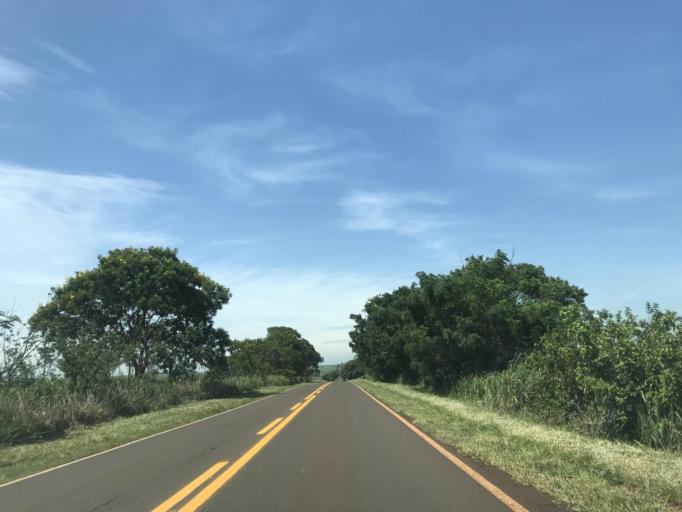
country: BR
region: Parana
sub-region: Terra Rica
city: Terra Rica
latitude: -22.8011
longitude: -52.6534
